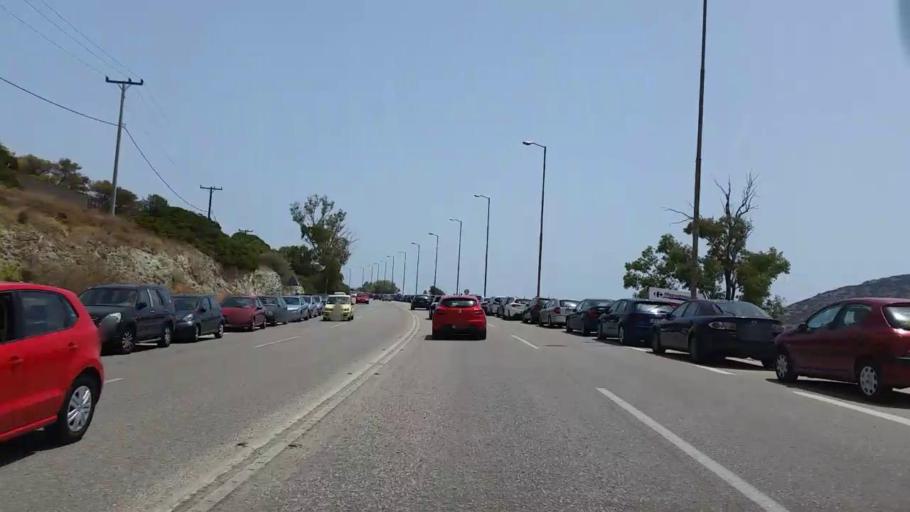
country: GR
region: Attica
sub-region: Nomarchia Anatolikis Attikis
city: Saronida
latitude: 37.7241
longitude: 23.9083
